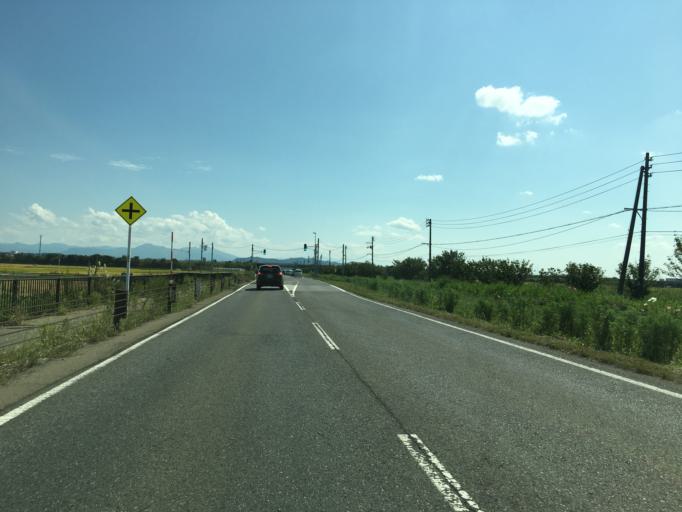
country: JP
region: Niigata
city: Niitsu-honcho
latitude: 37.8263
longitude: 139.0980
